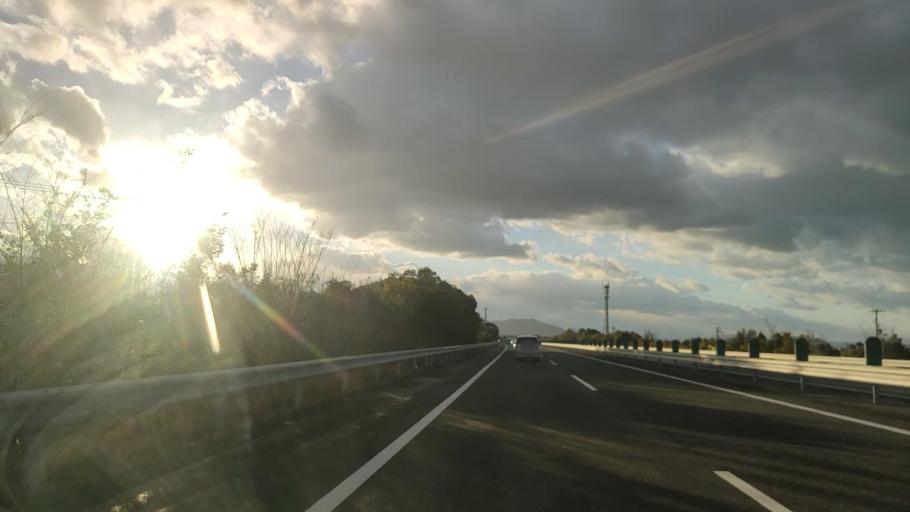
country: JP
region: Ehime
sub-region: Shikoku-chuo Shi
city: Matsuyama
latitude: 33.7856
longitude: 132.8582
